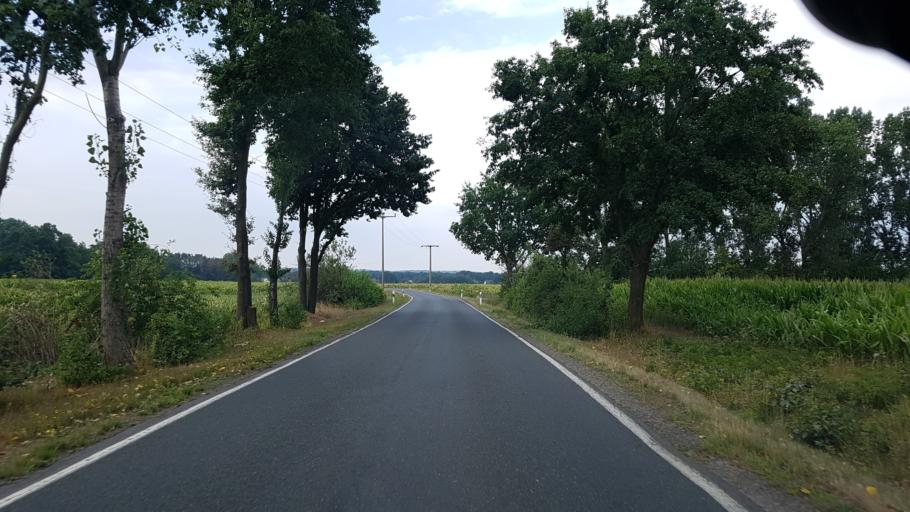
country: DE
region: Brandenburg
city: Lindenau
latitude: 51.4116
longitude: 13.7229
